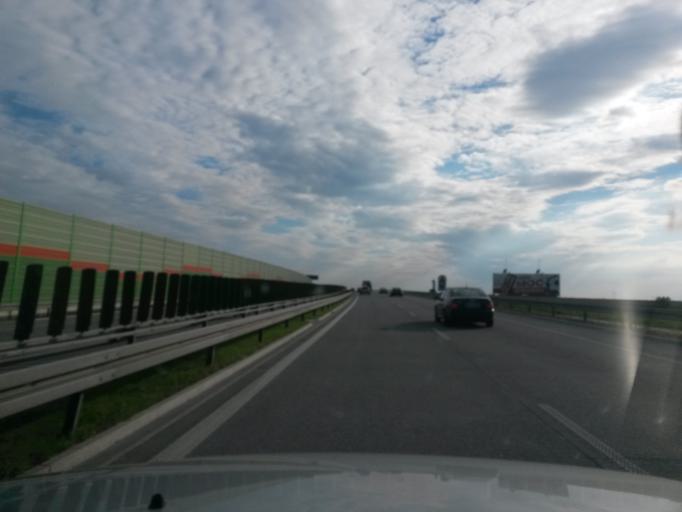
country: PL
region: Lodz Voivodeship
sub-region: Powiat tomaszowski
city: Tomaszow Mazowiecki
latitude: 51.5427
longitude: 19.9684
